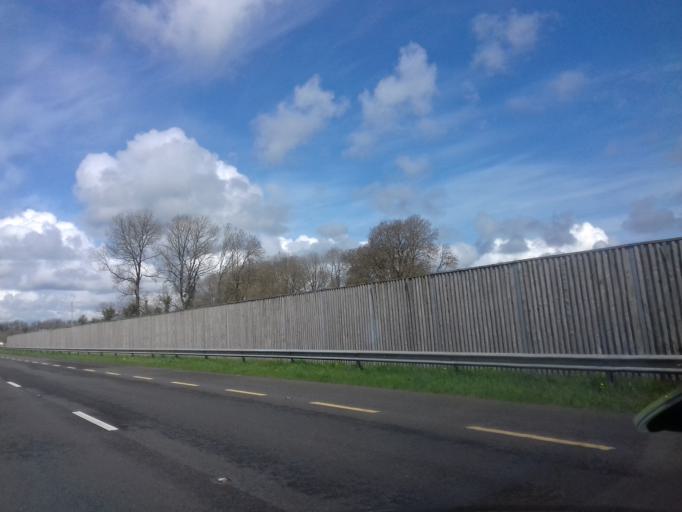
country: IE
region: Ulster
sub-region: An Cabhan
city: Belturbet
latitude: 54.0783
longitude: -7.4257
